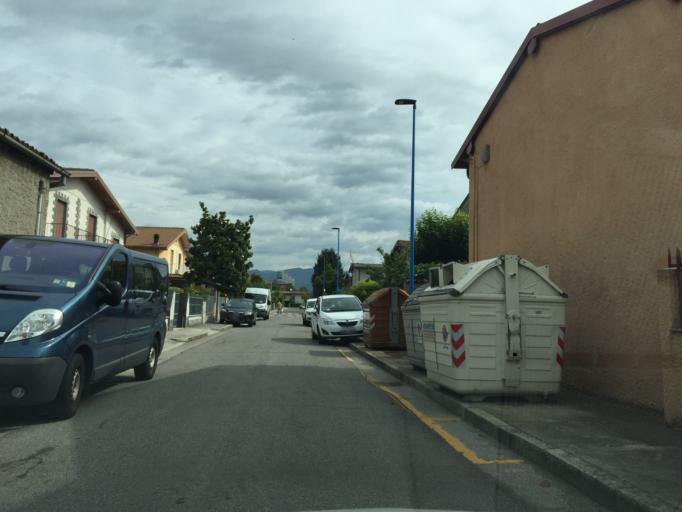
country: IT
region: Lombardy
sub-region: Provincia di Brescia
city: Folzano
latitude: 45.5099
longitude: 10.1909
